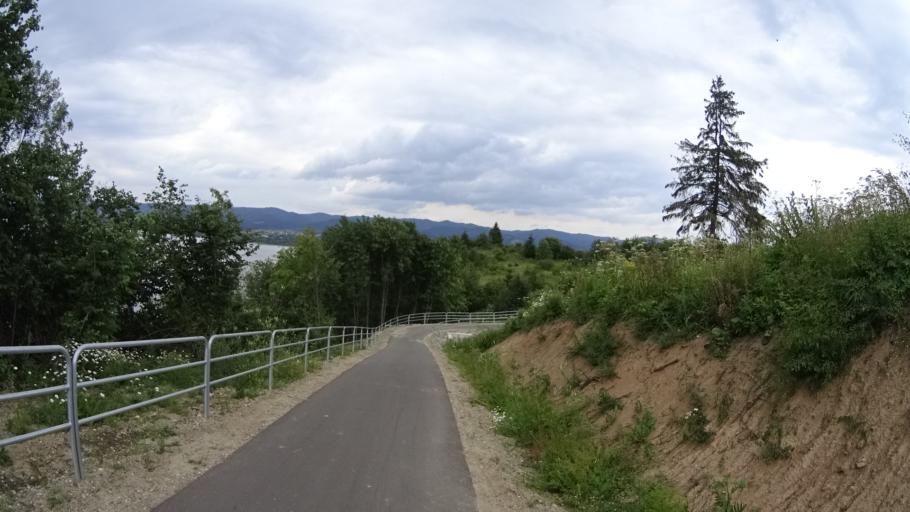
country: PL
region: Lesser Poland Voivodeship
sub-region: Powiat nowotarski
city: Maniowy
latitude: 49.4350
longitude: 20.2690
